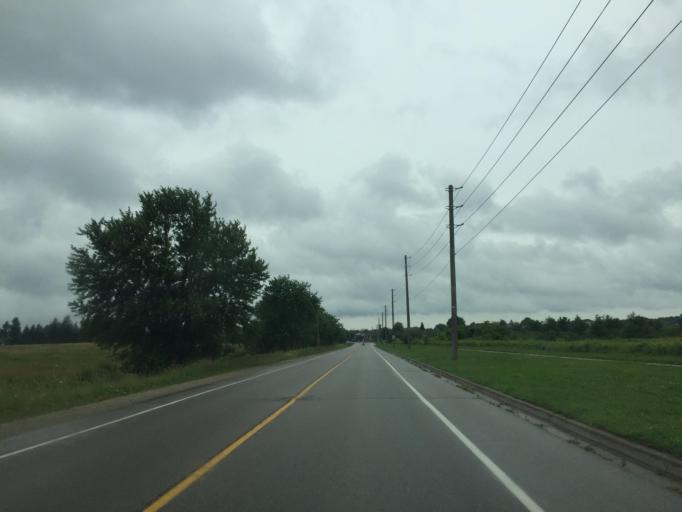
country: CA
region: Ontario
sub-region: Wellington County
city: Guelph
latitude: 43.4934
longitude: -80.2324
